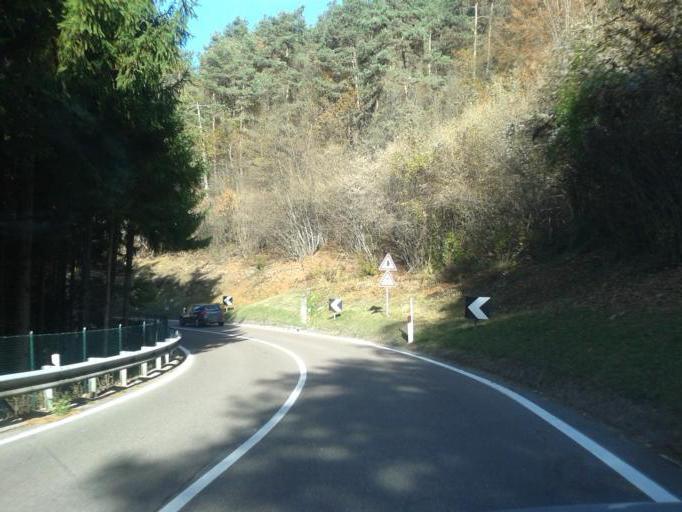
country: IT
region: Trentino-Alto Adige
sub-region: Provincia di Trento
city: Molina di Ledro
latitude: 45.8789
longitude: 10.7627
